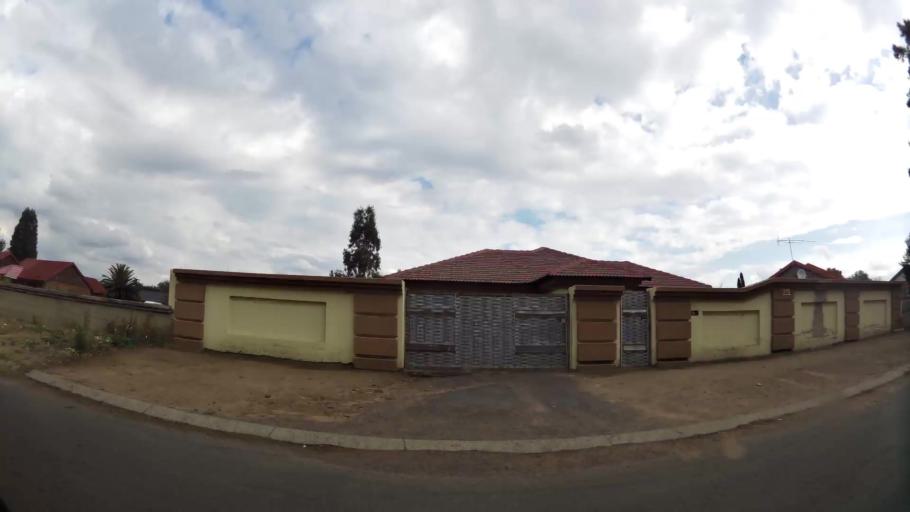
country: ZA
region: Gauteng
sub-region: Sedibeng District Municipality
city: Vanderbijlpark
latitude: -26.7071
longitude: 27.7983
